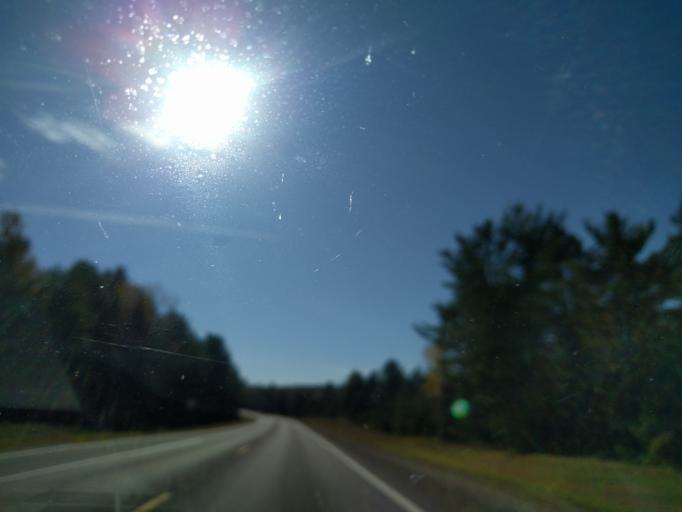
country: US
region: Michigan
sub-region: Marquette County
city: West Ishpeming
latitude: 46.4110
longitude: -87.9955
